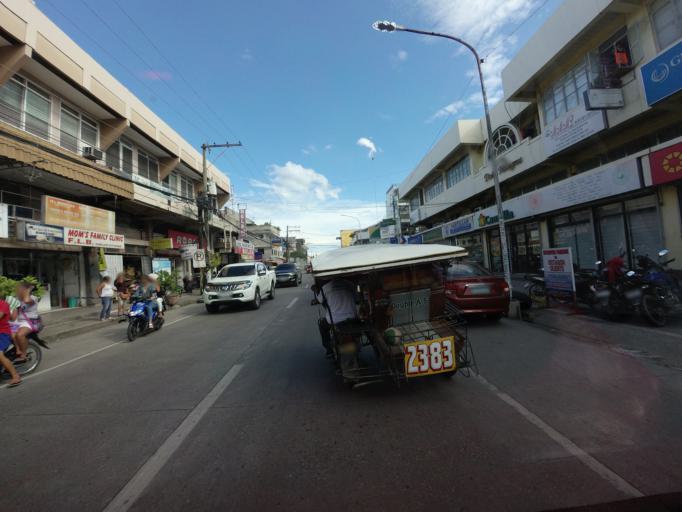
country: PH
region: Central Visayas
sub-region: Province of Negros Oriental
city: Dumaguete
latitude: 9.3042
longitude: 123.3078
